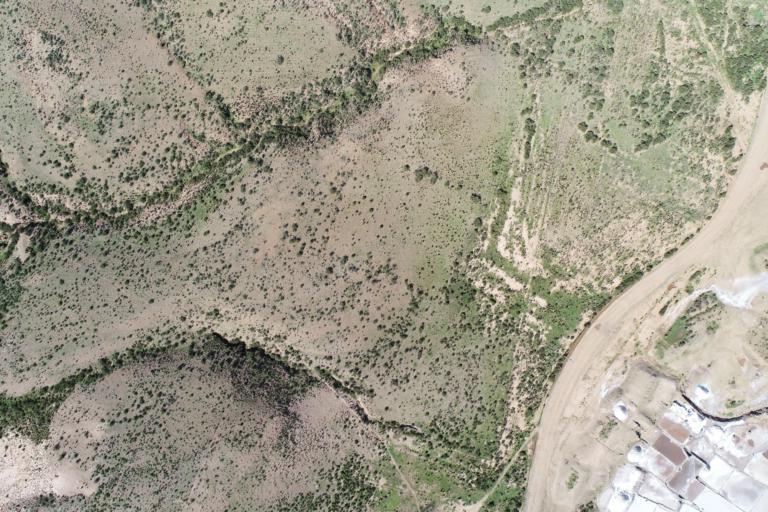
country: BO
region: La Paz
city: Curahuara de Carangas
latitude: -17.3020
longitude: -68.4850
